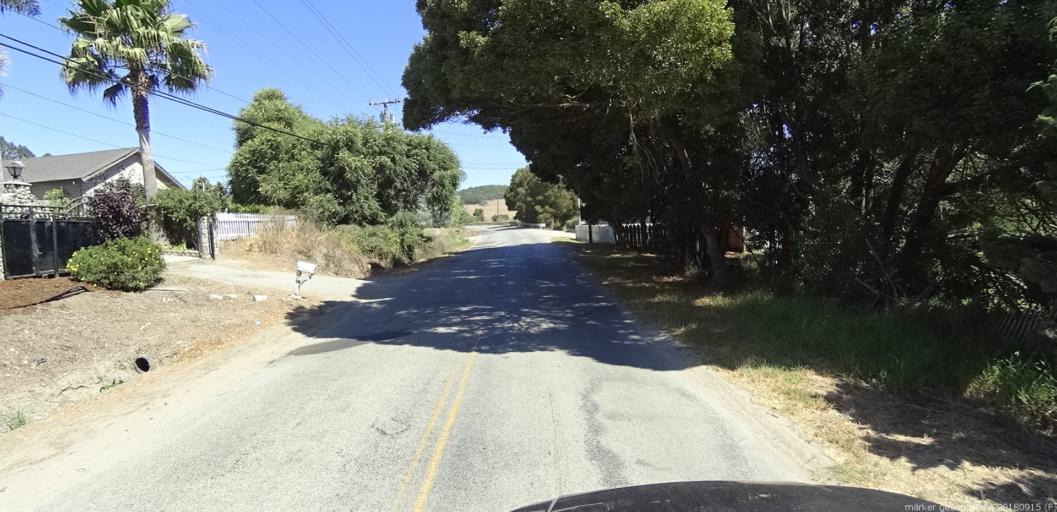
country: US
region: California
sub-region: Monterey County
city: Las Lomas
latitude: 36.8685
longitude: -121.7475
